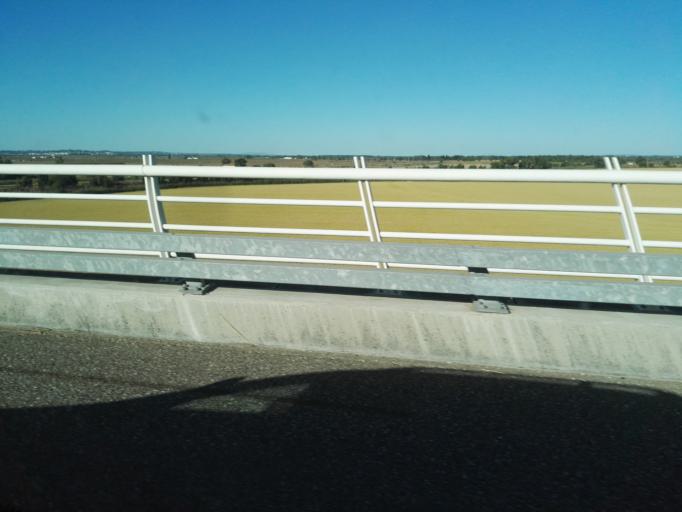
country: PT
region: Santarem
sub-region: Benavente
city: Samora Correia
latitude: 38.9728
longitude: -8.8739
